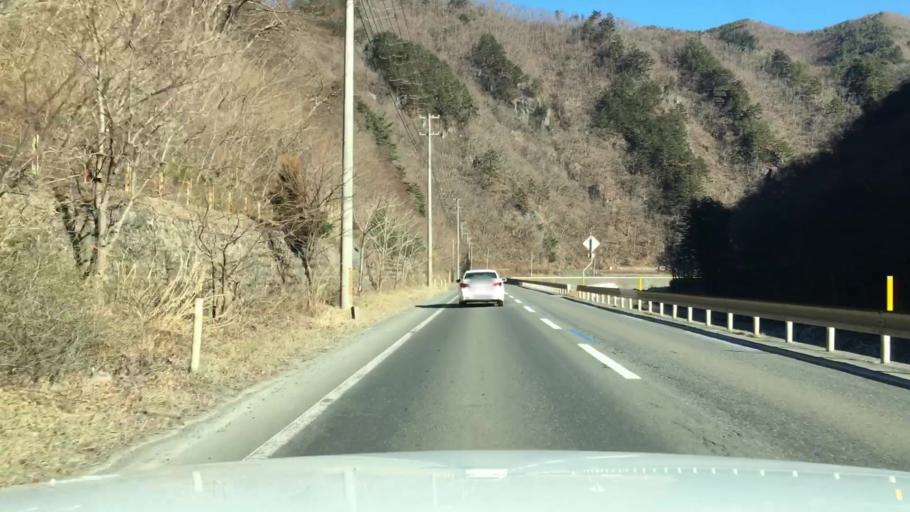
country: JP
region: Iwate
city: Miyako
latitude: 39.6067
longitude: 141.7721
